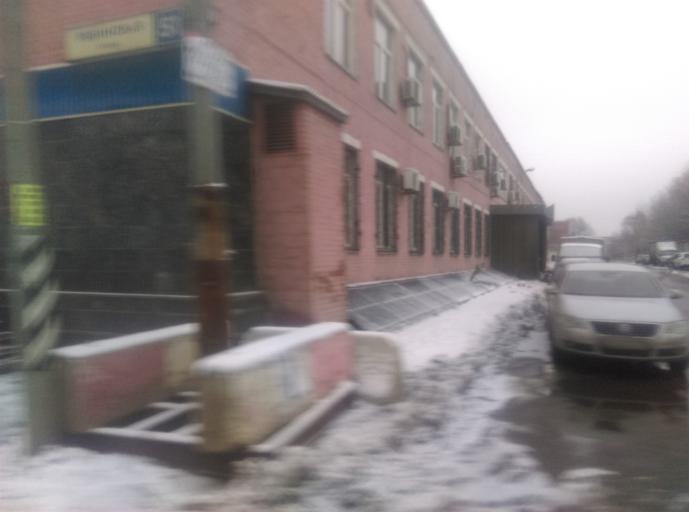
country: RU
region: Moscow
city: Mikhalkovo
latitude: 55.6939
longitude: 37.4256
